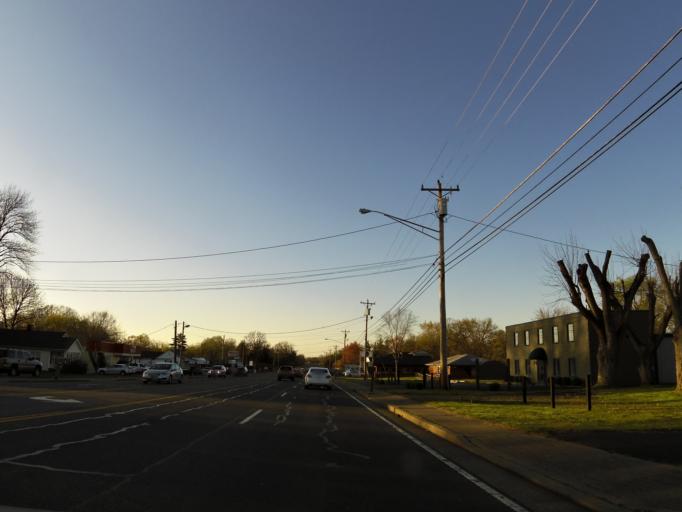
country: US
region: Tennessee
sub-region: Robertson County
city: Greenbrier
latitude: 36.4293
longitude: -86.8056
